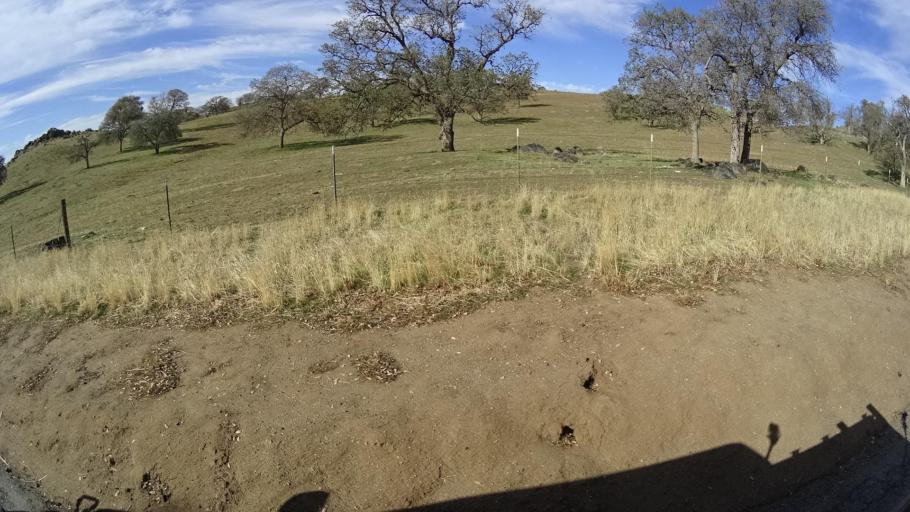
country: US
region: California
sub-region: Kern County
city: Oildale
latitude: 35.6011
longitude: -118.8249
